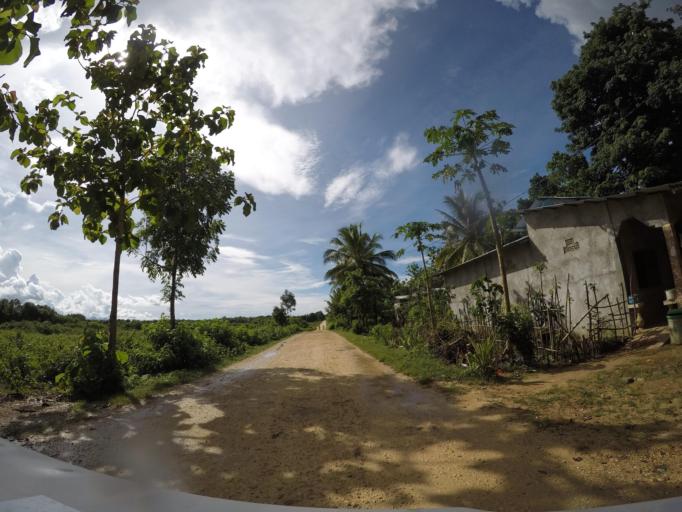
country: TL
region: Lautem
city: Lospalos
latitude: -8.5034
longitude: 127.0071
